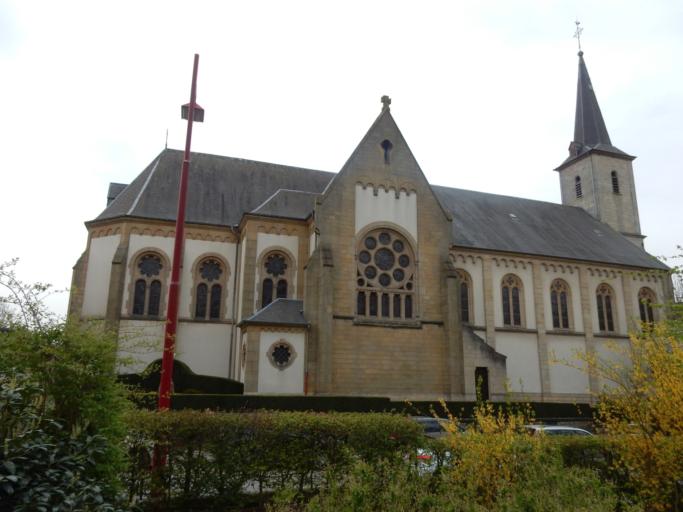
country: LU
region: Luxembourg
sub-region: Canton d'Esch-sur-Alzette
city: Petange
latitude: 49.5577
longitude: 5.8764
